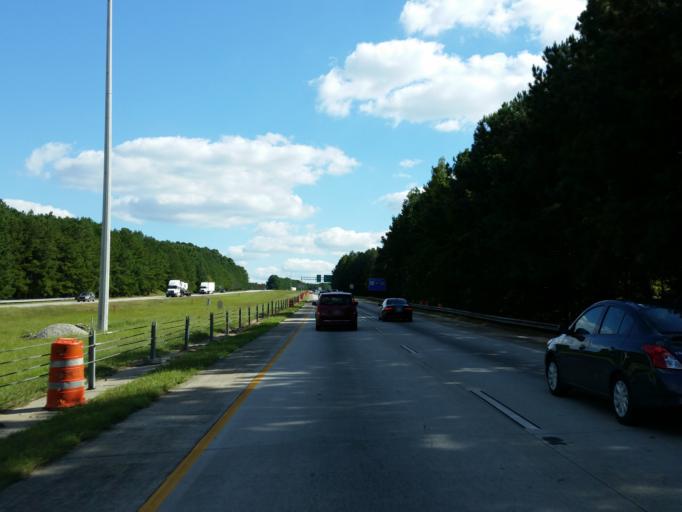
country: US
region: Georgia
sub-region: Henry County
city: Stockbridge
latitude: 33.5619
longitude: -84.2719
